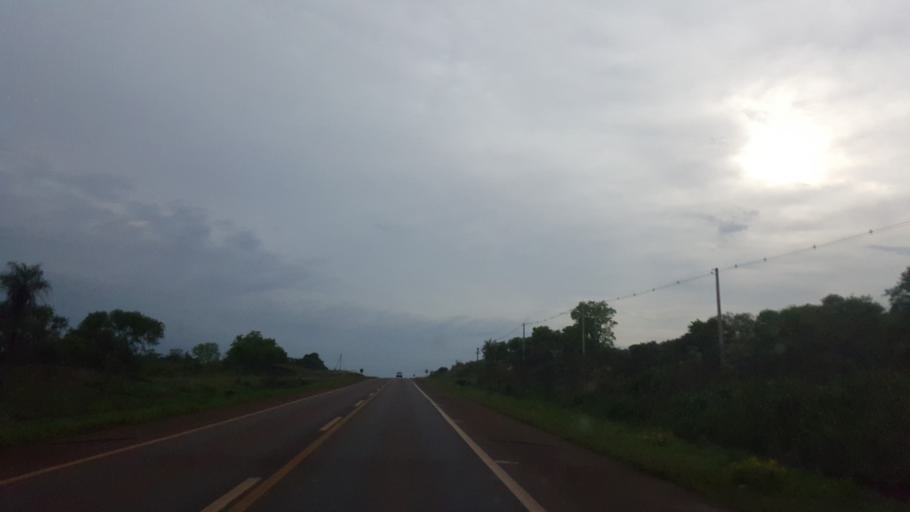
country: AR
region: Misiones
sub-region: Departamento de Apostoles
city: San Jose
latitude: -27.7625
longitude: -55.7943
